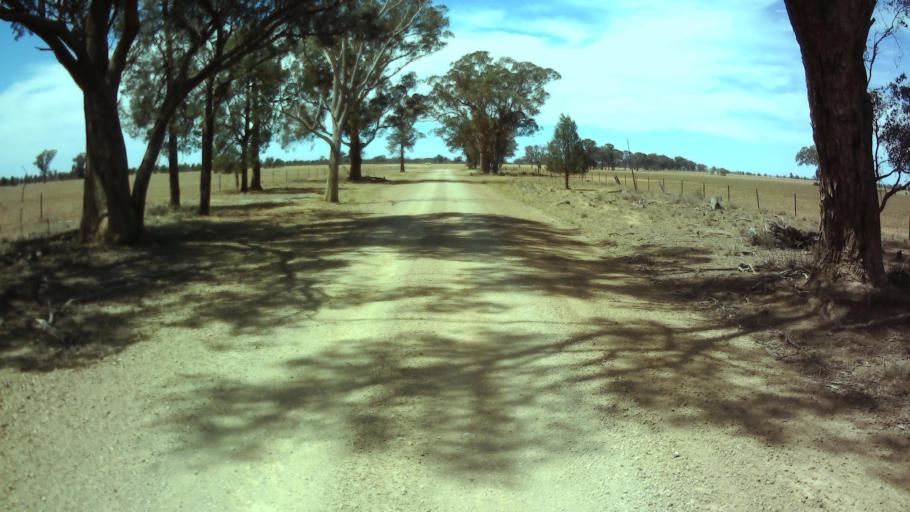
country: AU
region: New South Wales
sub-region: Weddin
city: Grenfell
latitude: -33.8623
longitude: 147.8066
